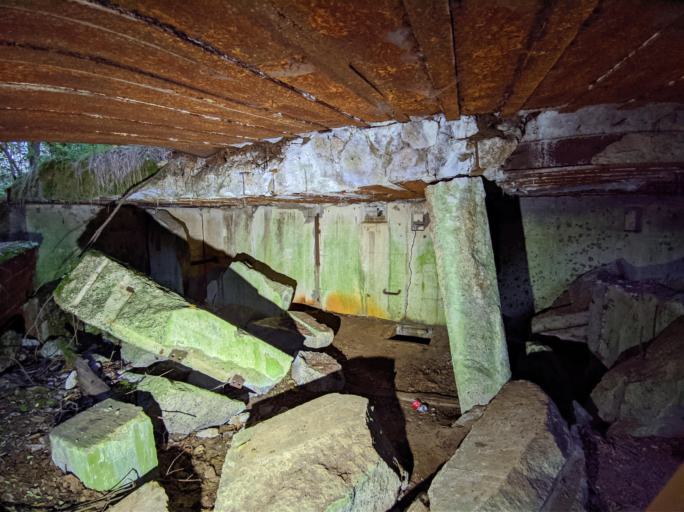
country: PL
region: Lubusz
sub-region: Powiat miedzyrzecki
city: Bledzew
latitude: 52.4368
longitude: 15.4691
